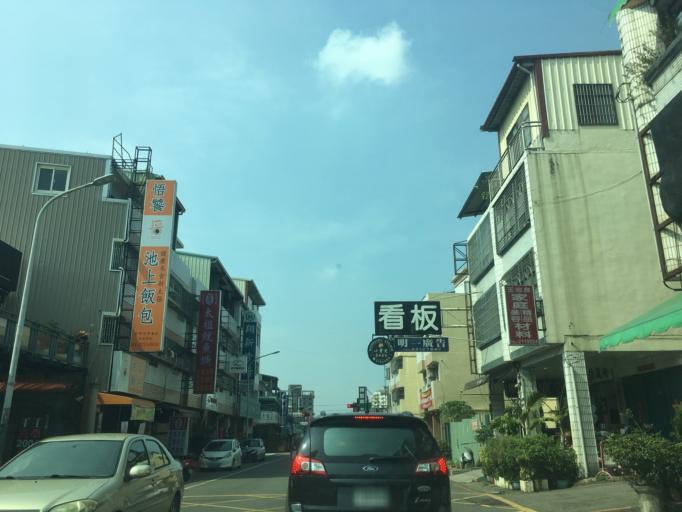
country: TW
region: Taiwan
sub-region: Taichung City
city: Taichung
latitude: 24.1489
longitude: 120.7103
